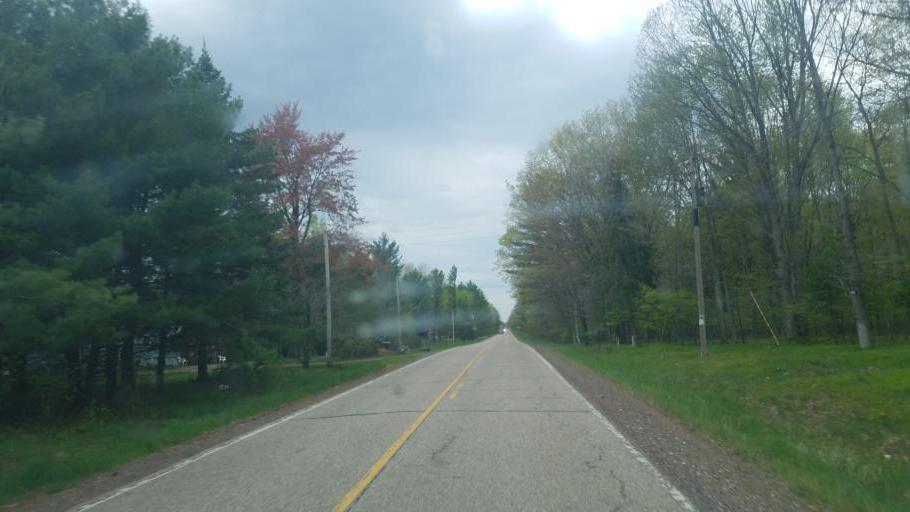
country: US
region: Wisconsin
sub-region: Wood County
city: Marshfield
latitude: 44.5126
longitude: -90.2830
